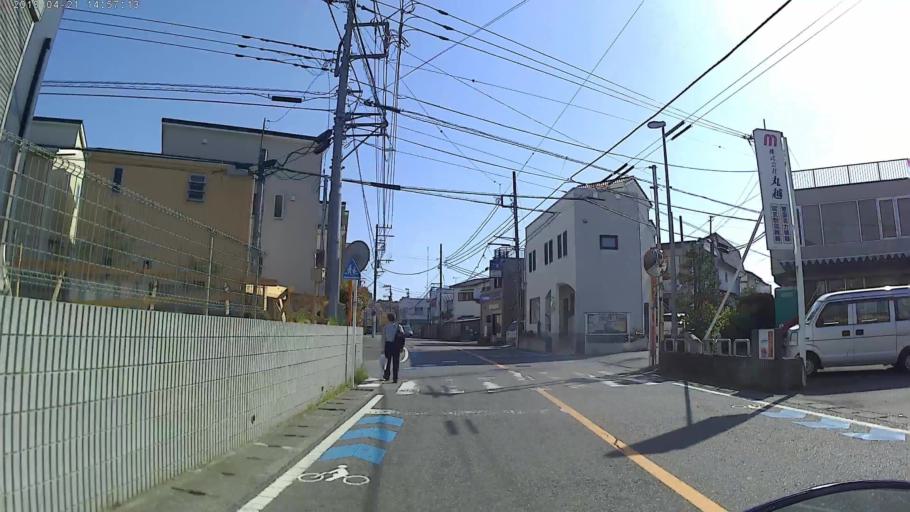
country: JP
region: Kanagawa
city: Chigasaki
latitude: 35.3210
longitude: 139.3876
